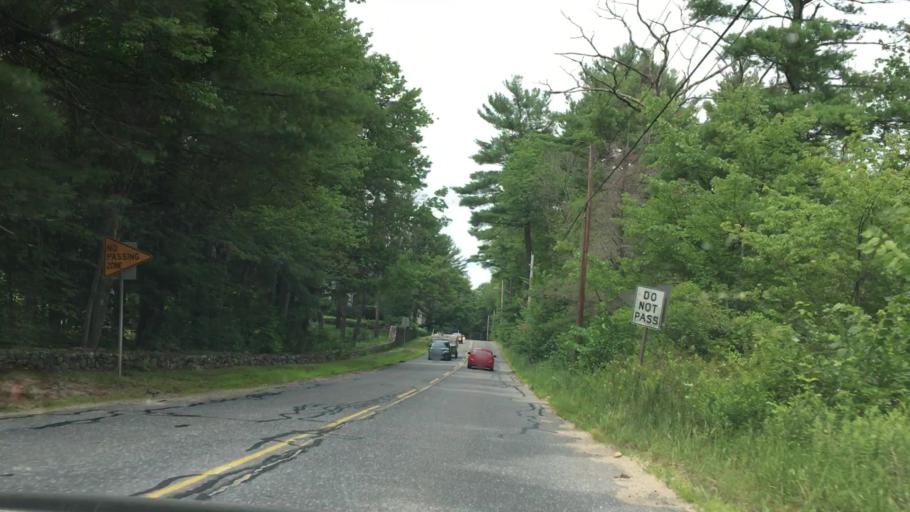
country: US
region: Massachusetts
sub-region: Worcester County
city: Winchendon
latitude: 42.6961
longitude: -72.0150
